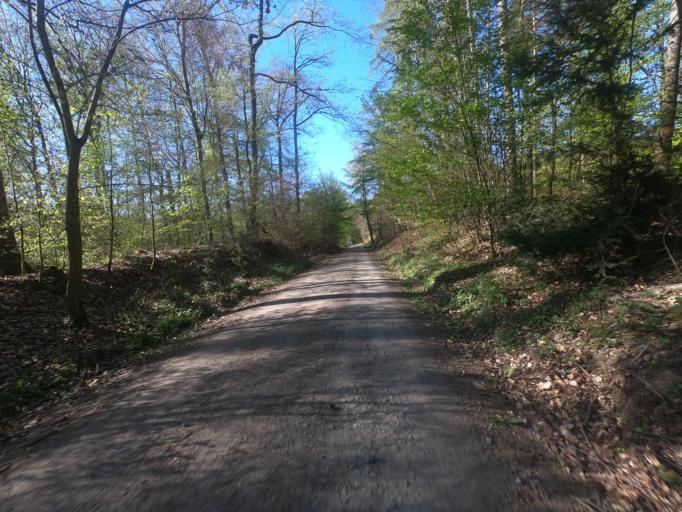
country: DE
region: Hesse
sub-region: Regierungsbezirk Darmstadt
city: Egelsbach
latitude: 49.9733
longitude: 8.7093
